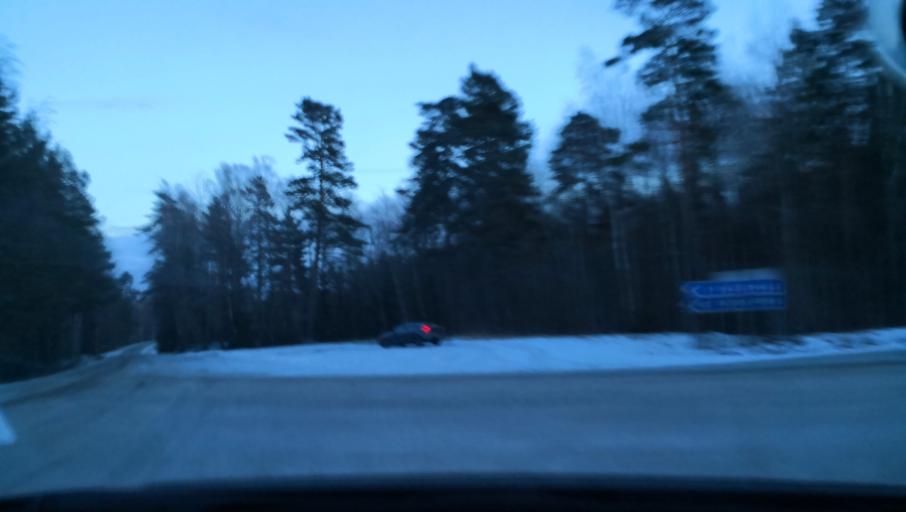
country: SE
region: Soedermanland
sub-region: Katrineholms Kommun
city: Katrineholm
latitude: 59.0834
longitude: 16.2222
